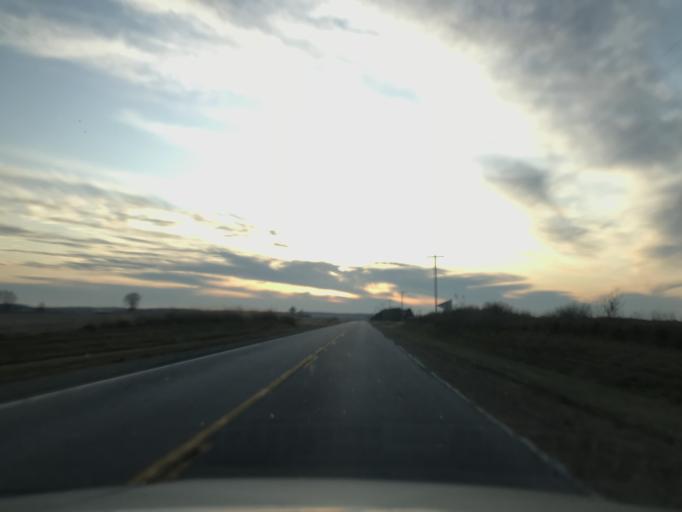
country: US
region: Illinois
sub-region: Warren County
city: Monmouth
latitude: 41.0236
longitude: -90.7812
